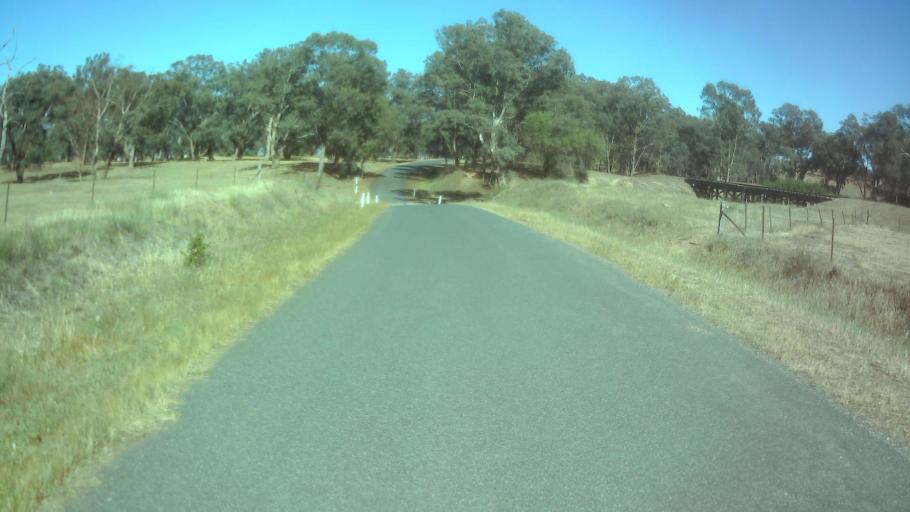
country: AU
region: New South Wales
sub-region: Weddin
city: Grenfell
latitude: -33.9972
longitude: 148.3959
